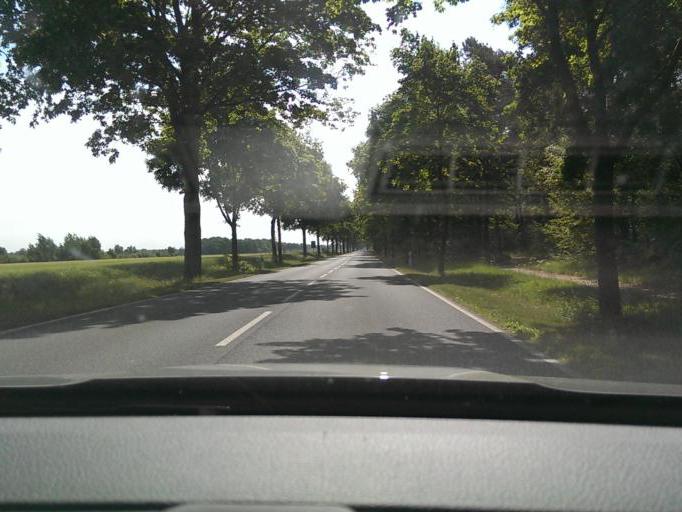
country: DE
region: Lower Saxony
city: Lindwedel
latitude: 52.6659
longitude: 9.7436
